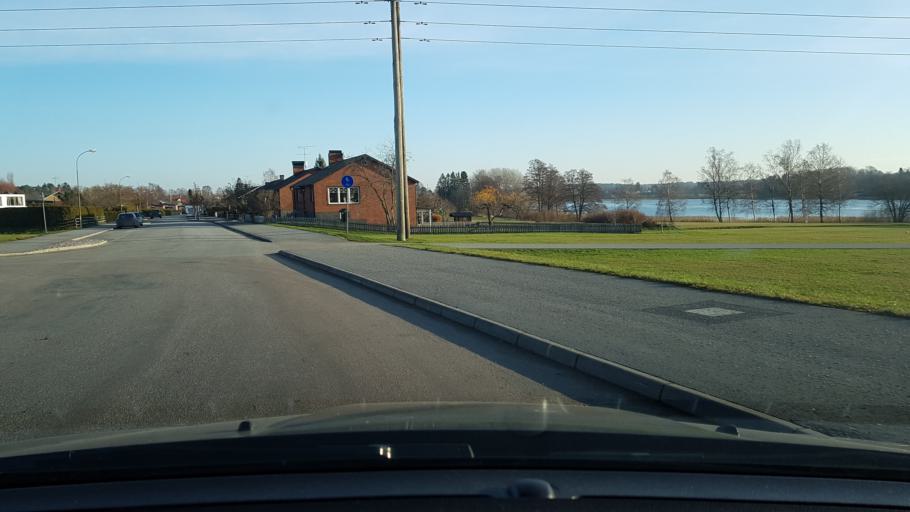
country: SE
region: Stockholm
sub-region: Norrtalje Kommun
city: Rimbo
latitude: 59.7404
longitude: 18.3452
